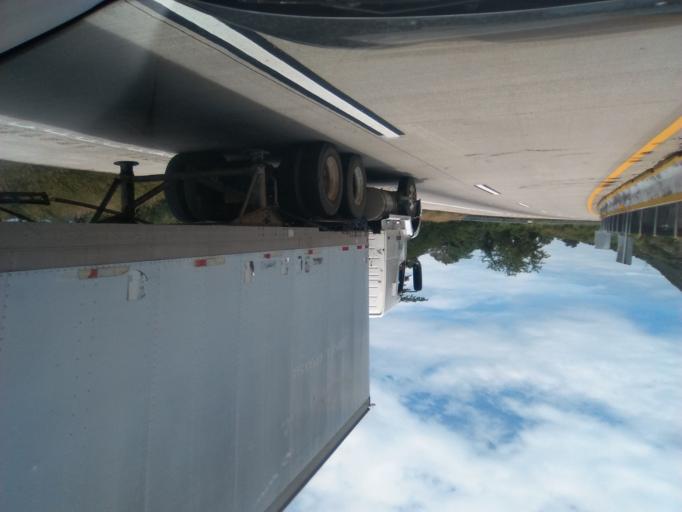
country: MX
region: Guerrero
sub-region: Chilpancingo de los Bravo
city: Julian Blanco (Dos Caminos)
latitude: 17.2159
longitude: -99.5301
